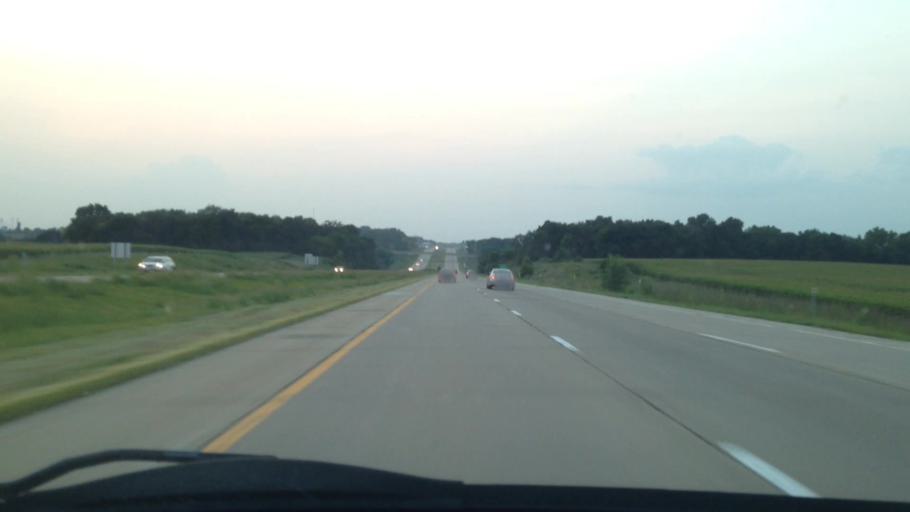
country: US
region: Iowa
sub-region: Benton County
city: Urbana
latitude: 42.3144
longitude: -91.9804
